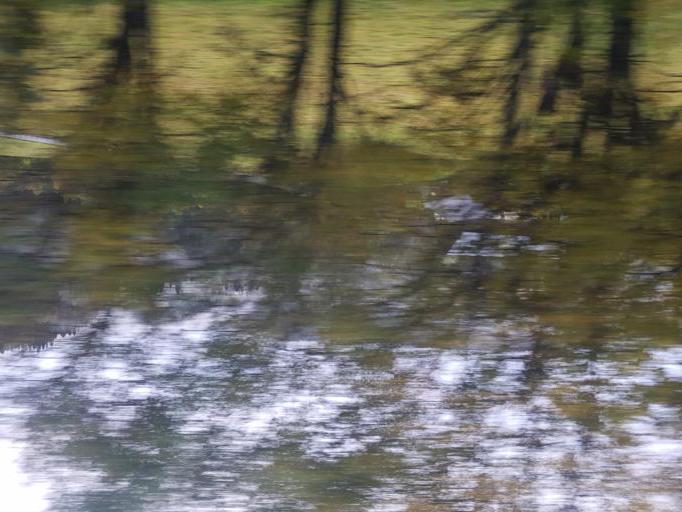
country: NO
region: Sor-Trondelag
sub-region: Melhus
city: Lundamo
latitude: 63.1821
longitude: 10.3118
